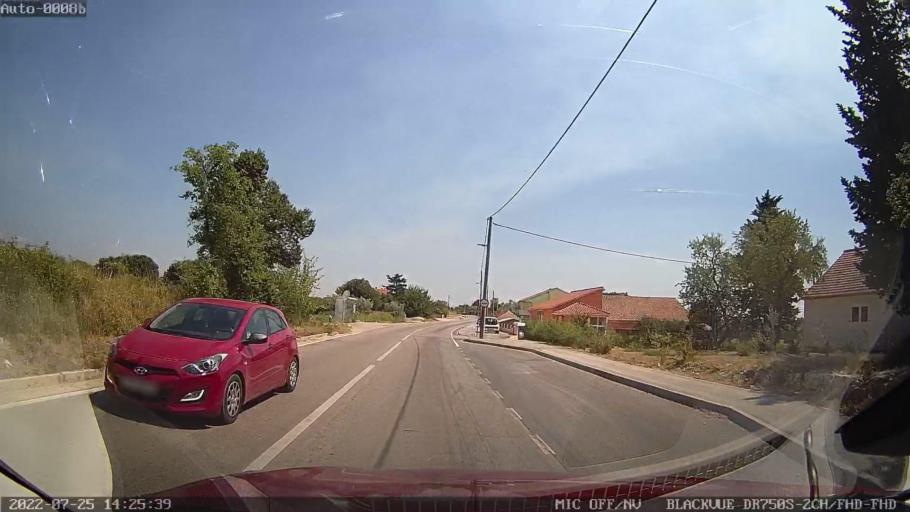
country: HR
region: Zadarska
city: Policnik
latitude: 44.1434
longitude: 15.3328
